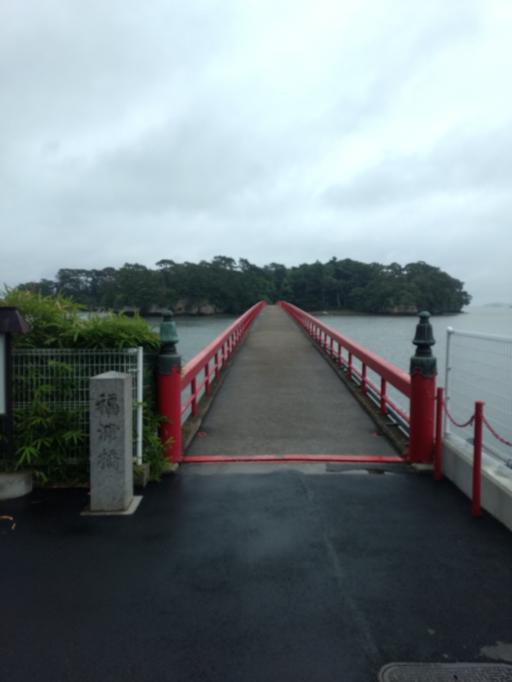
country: JP
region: Miyagi
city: Matsushima
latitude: 38.3700
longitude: 141.0682
